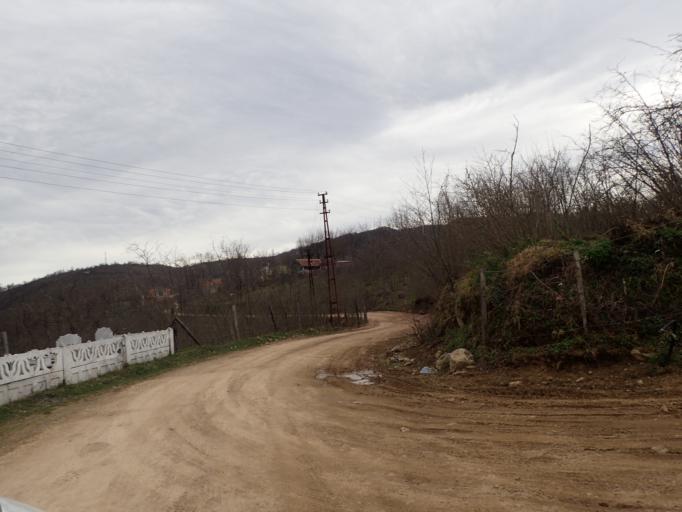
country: TR
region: Ordu
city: Camas
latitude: 40.8904
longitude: 37.5185
